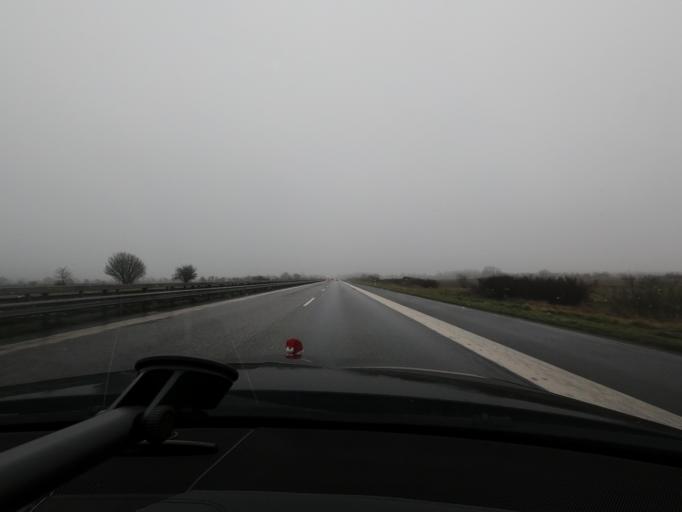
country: DE
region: Schleswig-Holstein
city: Lottorf
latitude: 54.4369
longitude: 9.5928
